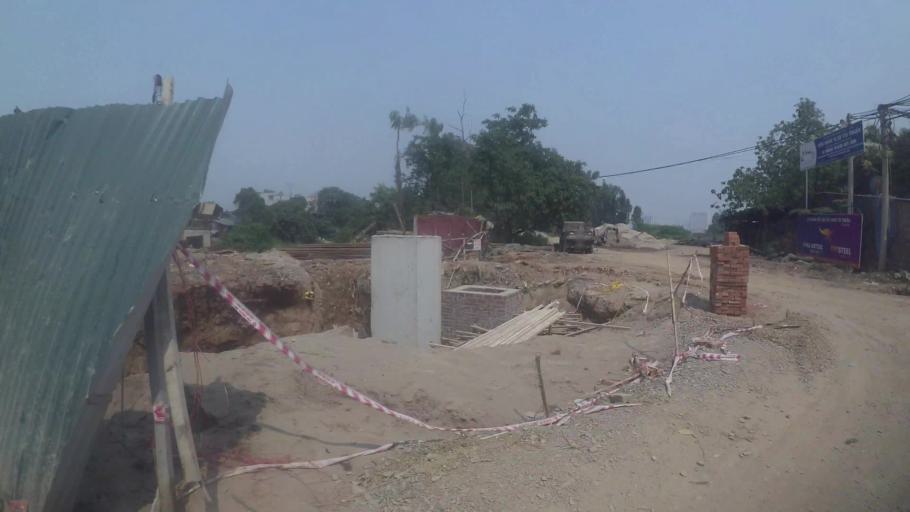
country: VN
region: Ha Noi
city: Ha Dong
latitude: 20.9966
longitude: 105.7626
